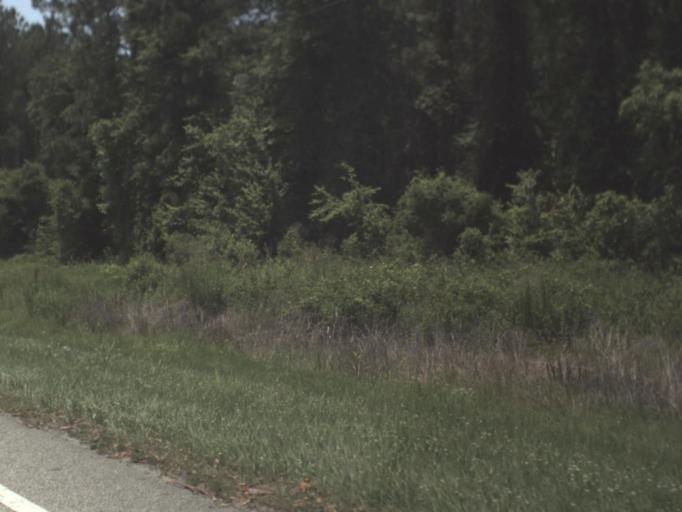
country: US
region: Florida
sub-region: Baker County
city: Macclenny
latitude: 30.1472
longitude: -82.0347
